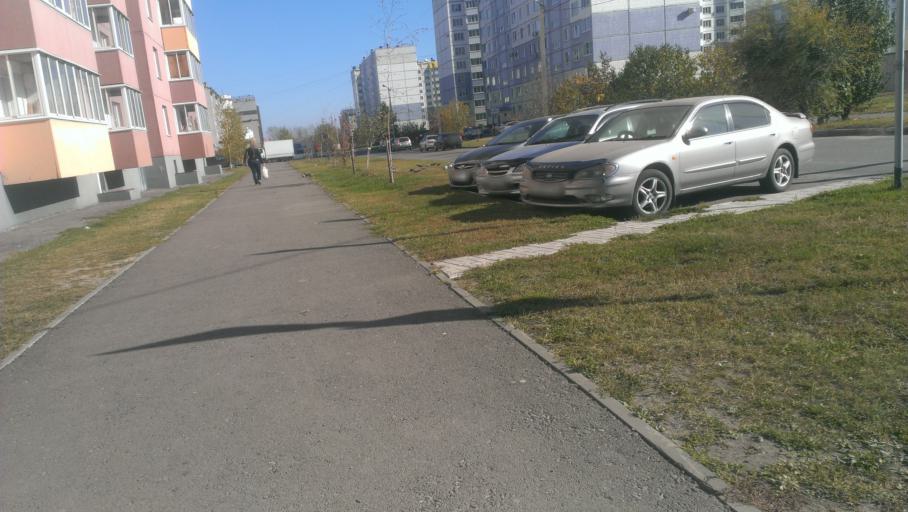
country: RU
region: Altai Krai
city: Novosilikatnyy
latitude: 53.3299
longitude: 83.6843
